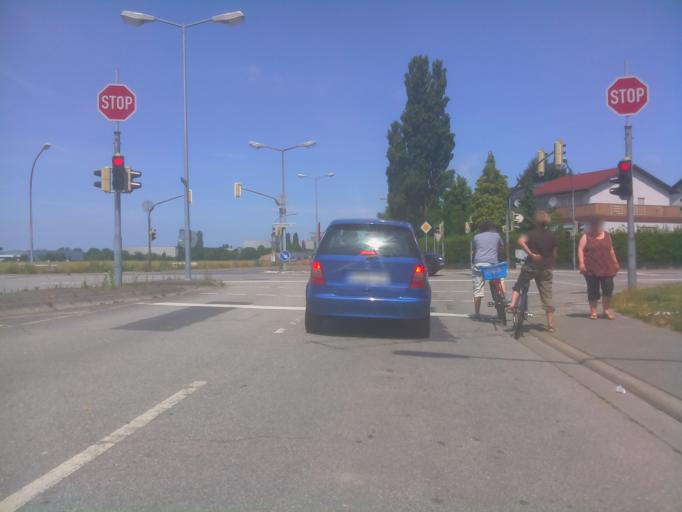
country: DE
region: Hesse
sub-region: Regierungsbezirk Darmstadt
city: Heppenheim an der Bergstrasse
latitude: 49.6290
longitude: 8.6227
